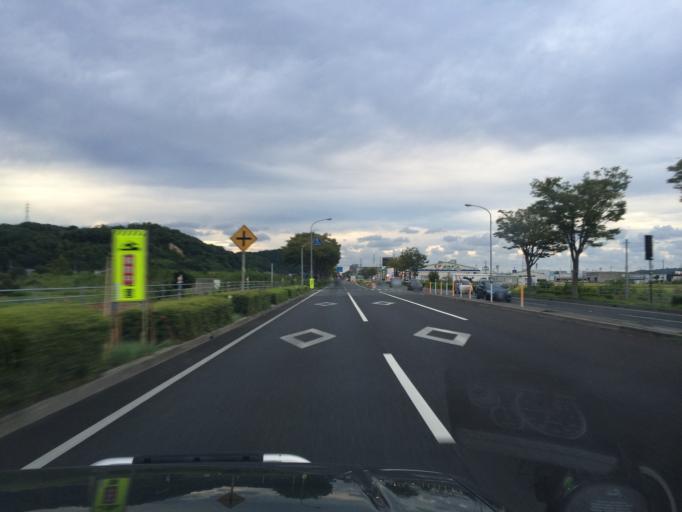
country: JP
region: Tottori
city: Tottori
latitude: 35.4860
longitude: 134.2049
